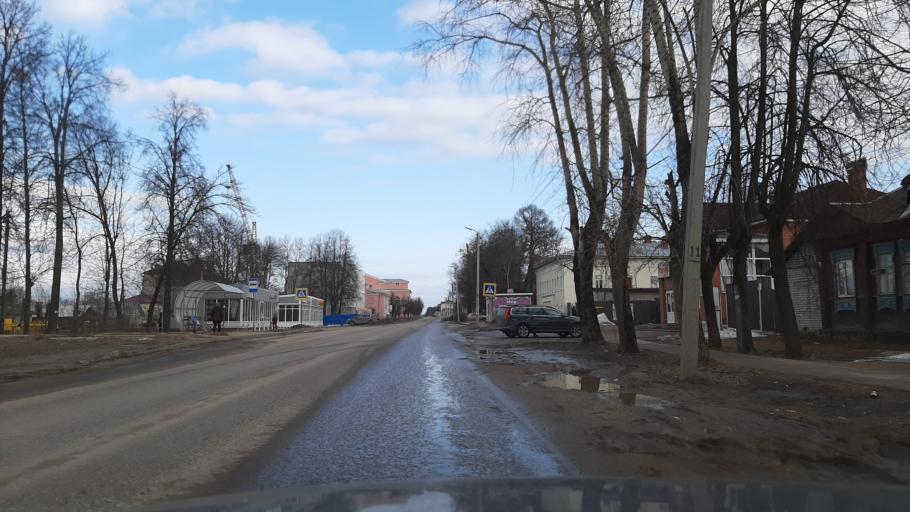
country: RU
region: Ivanovo
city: Teykovo
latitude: 56.8546
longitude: 40.5283
